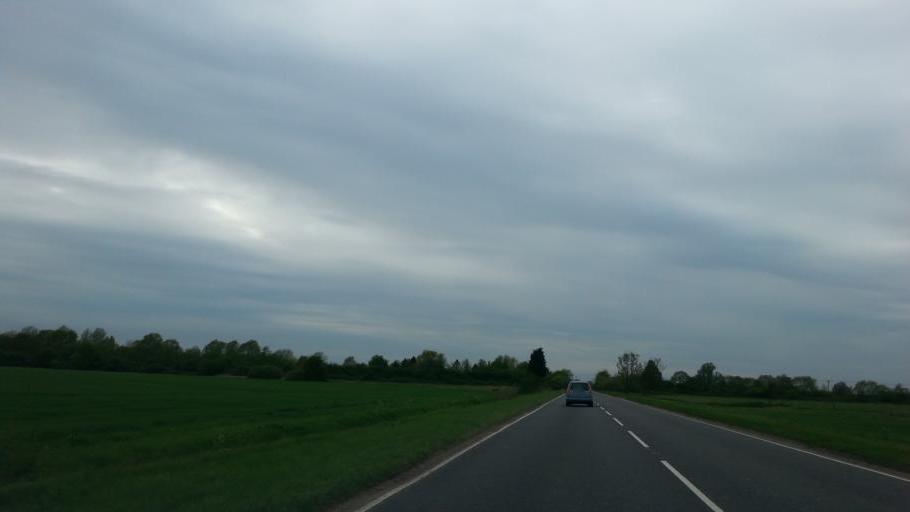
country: GB
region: England
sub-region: Cambridgeshire
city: March
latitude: 52.5265
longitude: 0.0780
